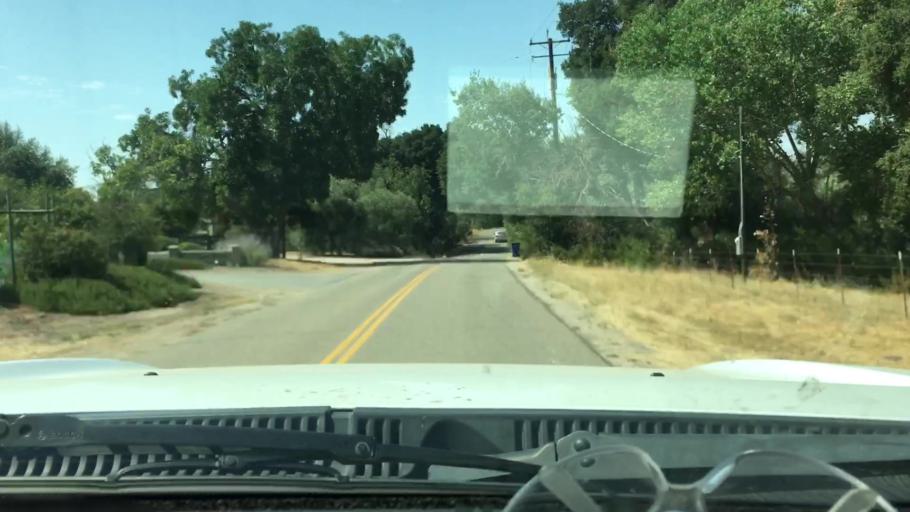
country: US
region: California
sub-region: San Luis Obispo County
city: Atascadero
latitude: 35.5303
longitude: -120.6181
